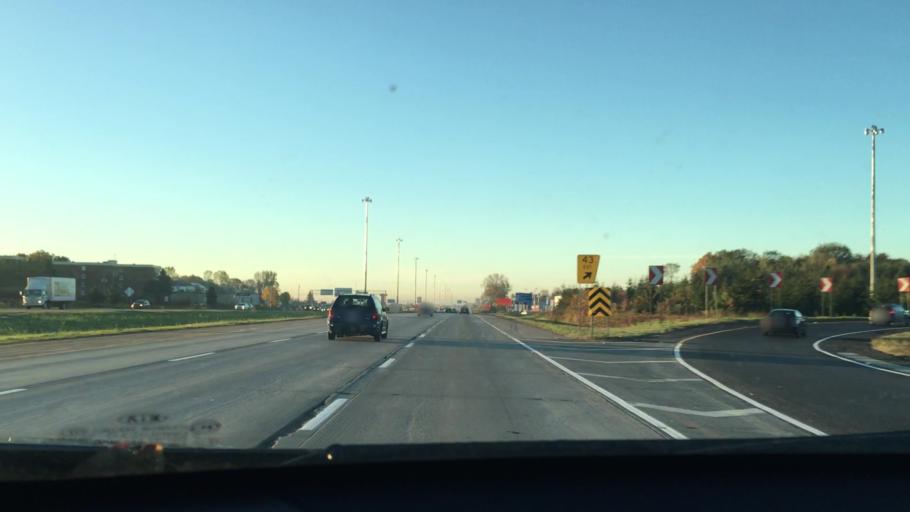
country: CA
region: Quebec
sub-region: Laurentides
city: Saint-Jerome
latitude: 45.7777
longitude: -74.0209
